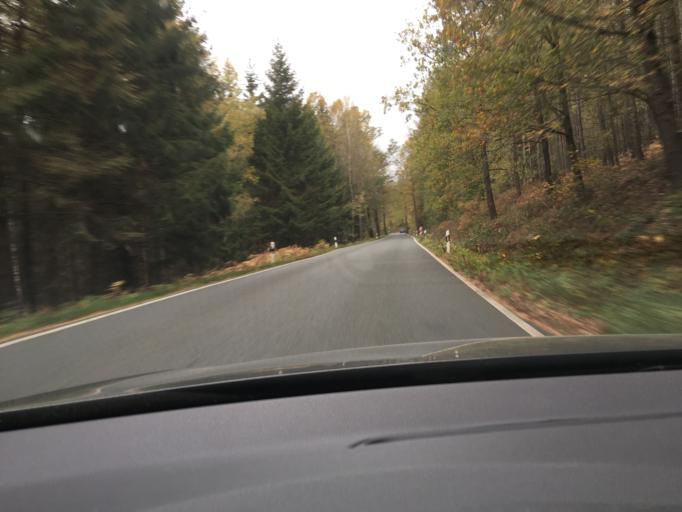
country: DE
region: Saxony
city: Reinhardtsgrimma
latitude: 50.8943
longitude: 13.7848
